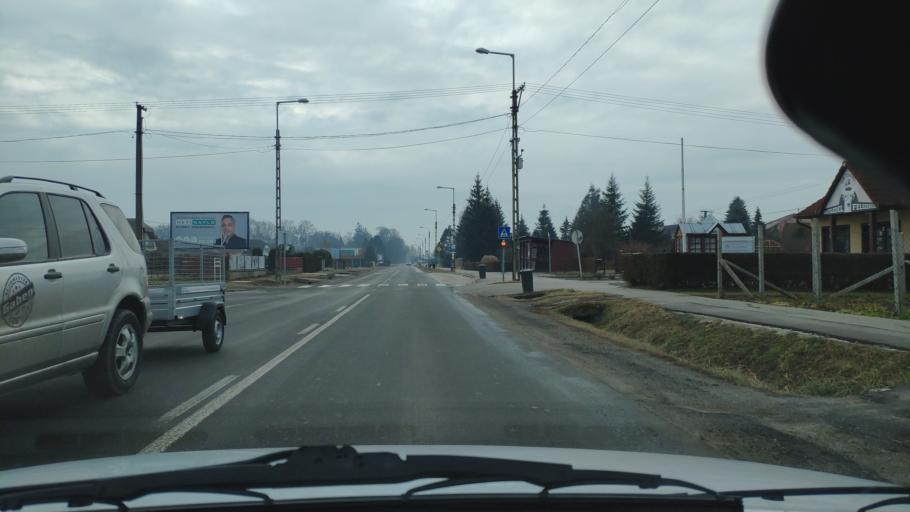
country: HU
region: Zala
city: Nagykanizsa
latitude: 46.4840
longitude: 16.9854
